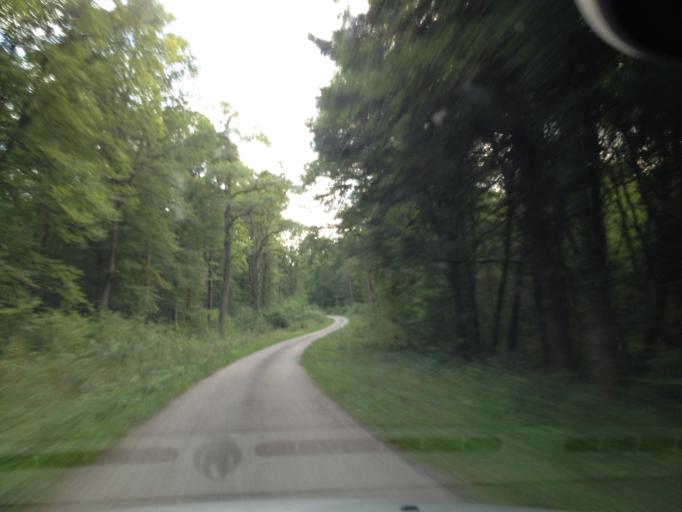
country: FR
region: Lorraine
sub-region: Departement des Vosges
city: Bains-les-Bains
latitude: 47.9494
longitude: 6.1764
